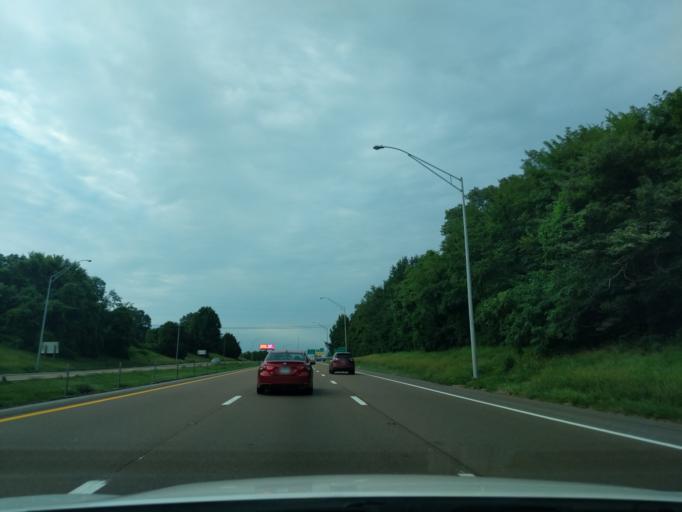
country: US
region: Tennessee
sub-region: Shelby County
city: New South Memphis
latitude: 35.1028
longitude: -90.0761
